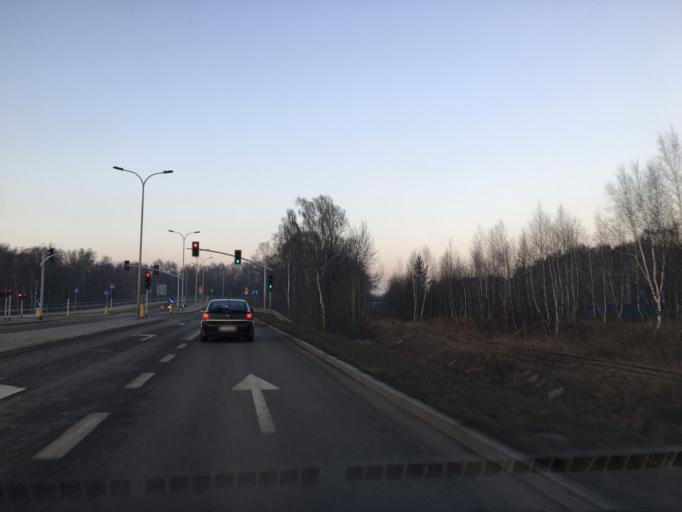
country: PL
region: Silesian Voivodeship
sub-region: Powiat tarnogorski
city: Radzionkow
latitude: 50.3679
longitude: 18.8766
